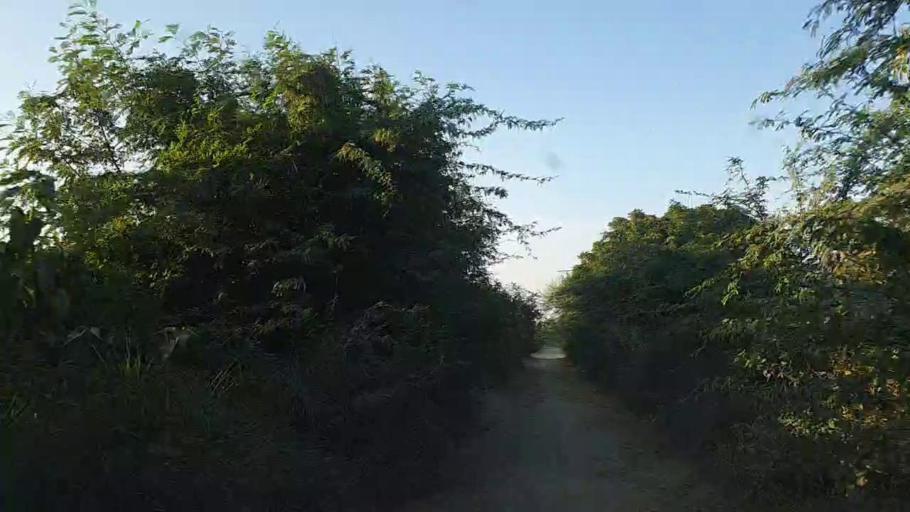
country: PK
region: Sindh
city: Mirpur Batoro
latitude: 24.7285
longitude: 68.2120
